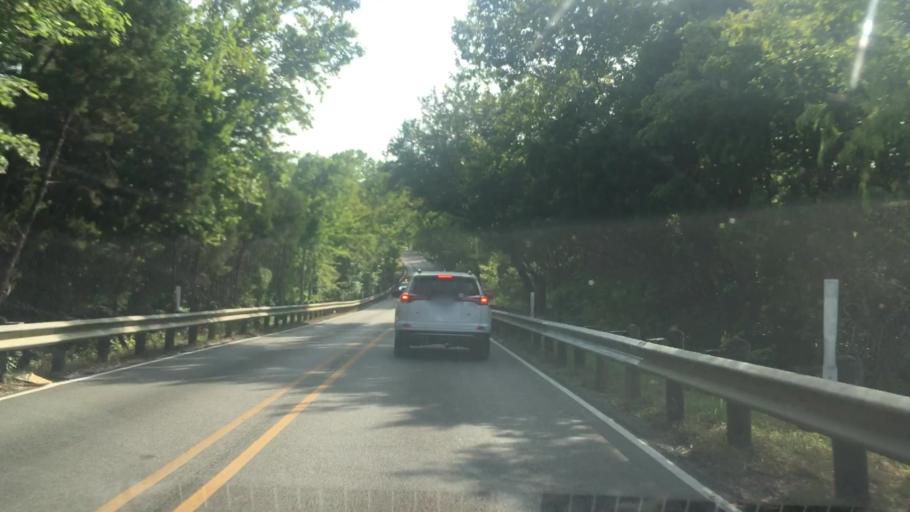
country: US
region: Texas
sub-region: Williamson County
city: Anderson Mill
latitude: 30.4520
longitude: -97.8504
